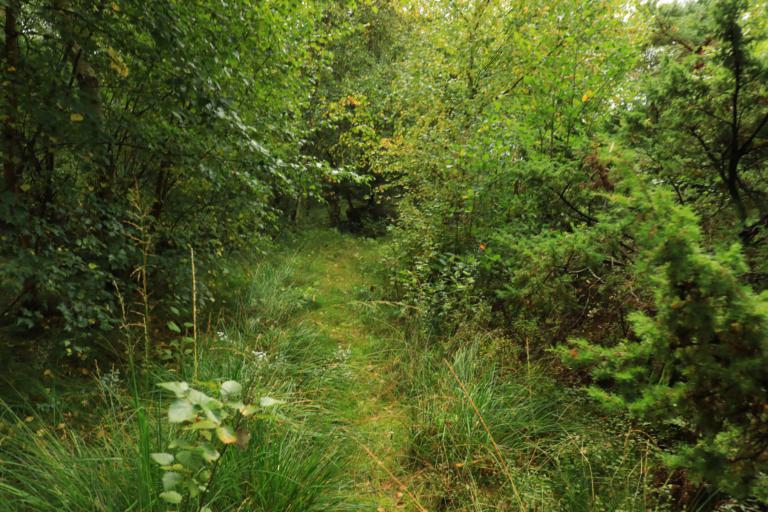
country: SE
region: Halland
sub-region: Varbergs Kommun
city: Traslovslage
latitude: 57.0755
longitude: 12.2697
